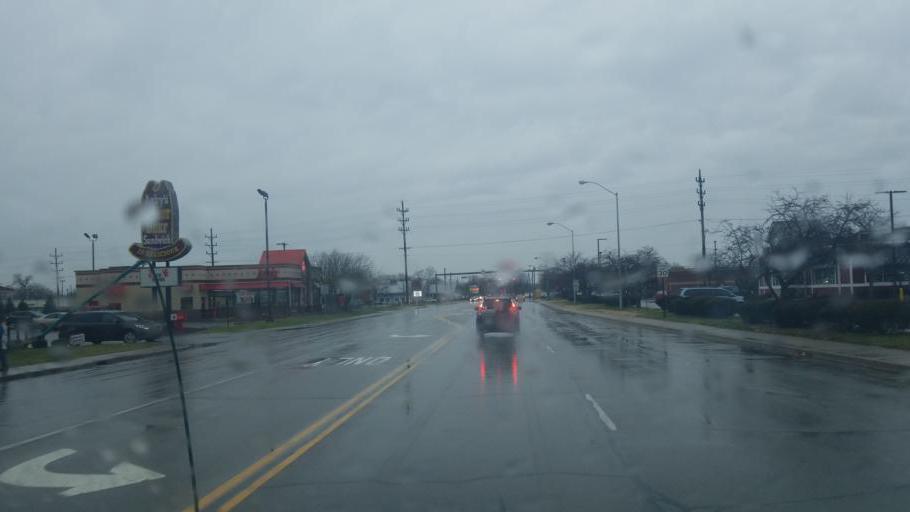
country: US
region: Indiana
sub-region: Bartholomew County
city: Columbus
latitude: 39.2231
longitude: -85.9018
